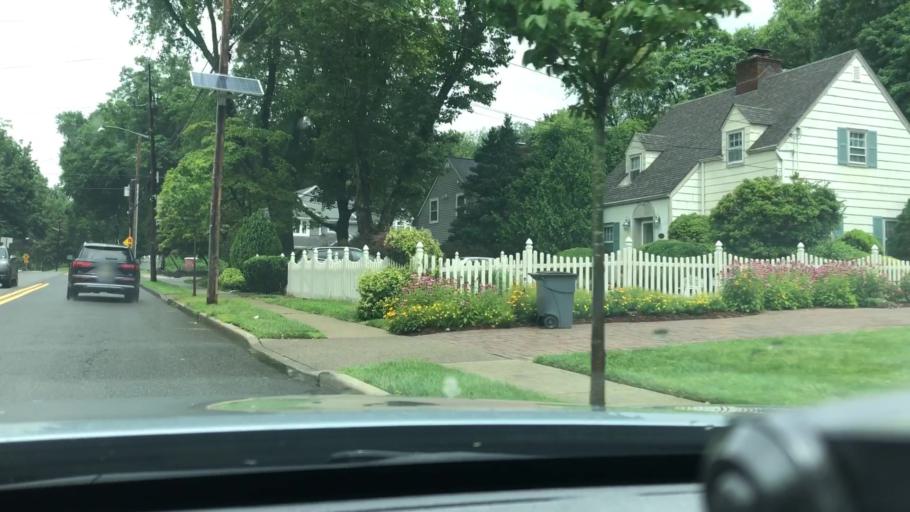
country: US
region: New Jersey
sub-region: Bergen County
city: Ho-Ho-Kus
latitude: 41.0066
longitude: -74.1069
